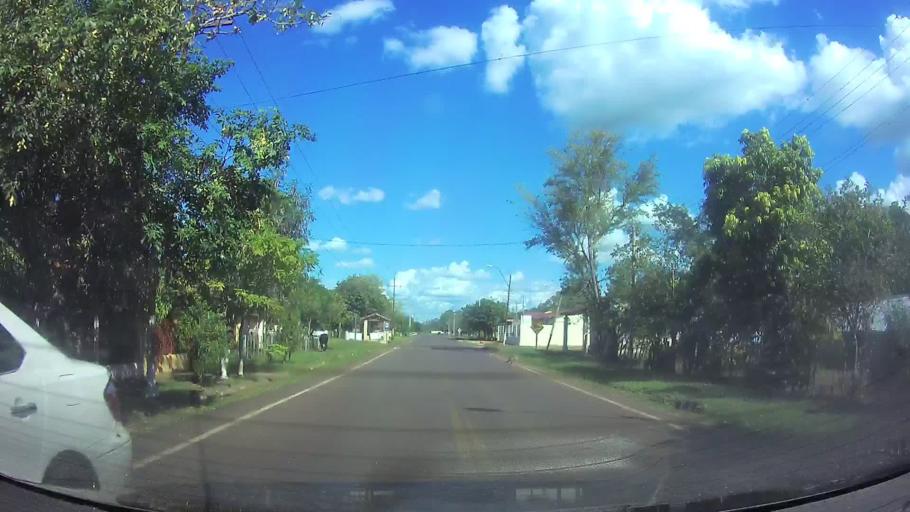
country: PY
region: Paraguari
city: Sapucai
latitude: -25.6868
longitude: -56.8627
